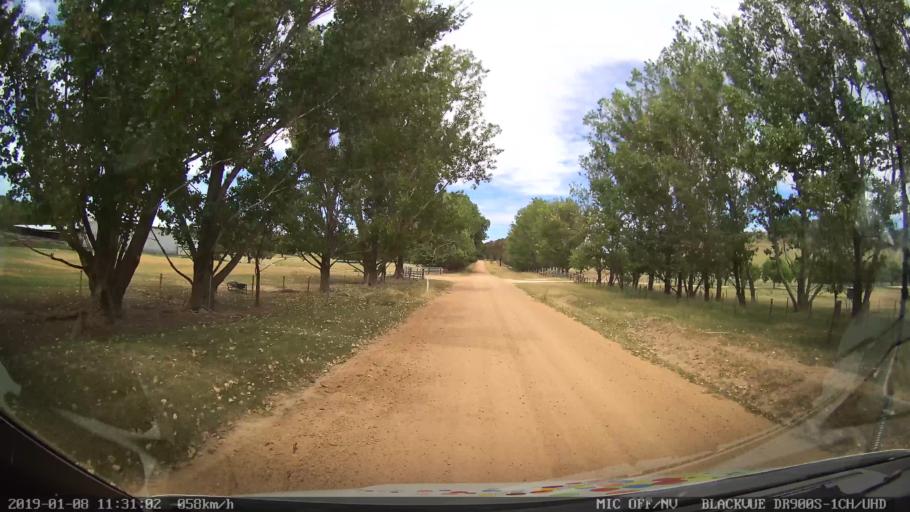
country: AU
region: New South Wales
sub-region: Guyra
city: Guyra
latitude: -30.3106
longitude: 151.5406
